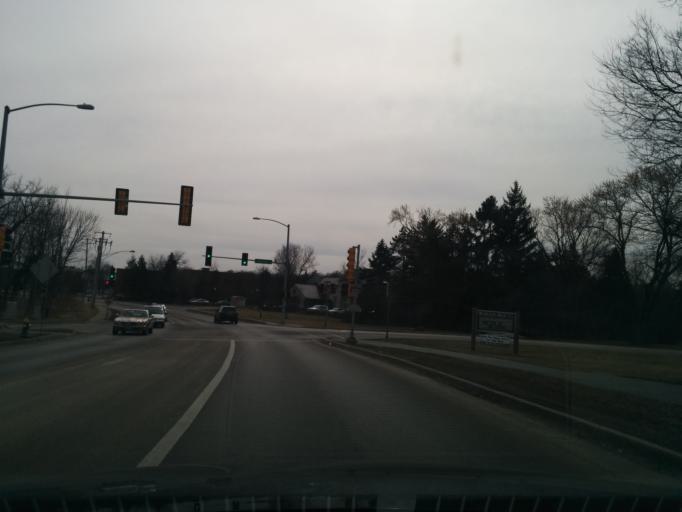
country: US
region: Illinois
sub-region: DuPage County
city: Oak Brook
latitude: 41.8199
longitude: -87.9273
